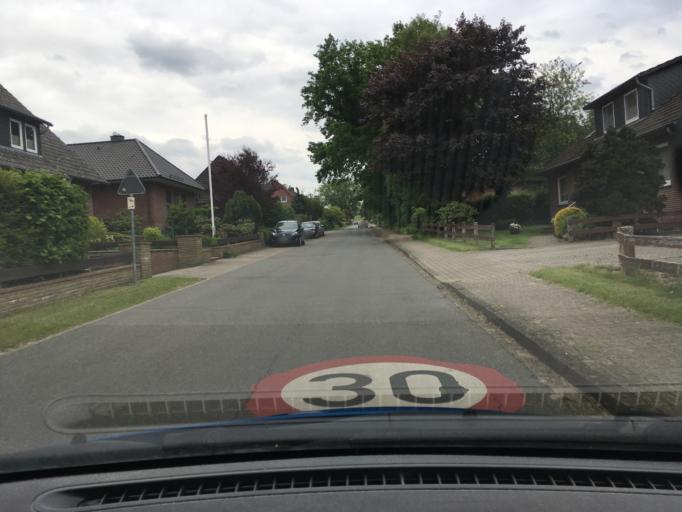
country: DE
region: Lower Saxony
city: Eyendorf
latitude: 53.2053
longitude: 10.1615
